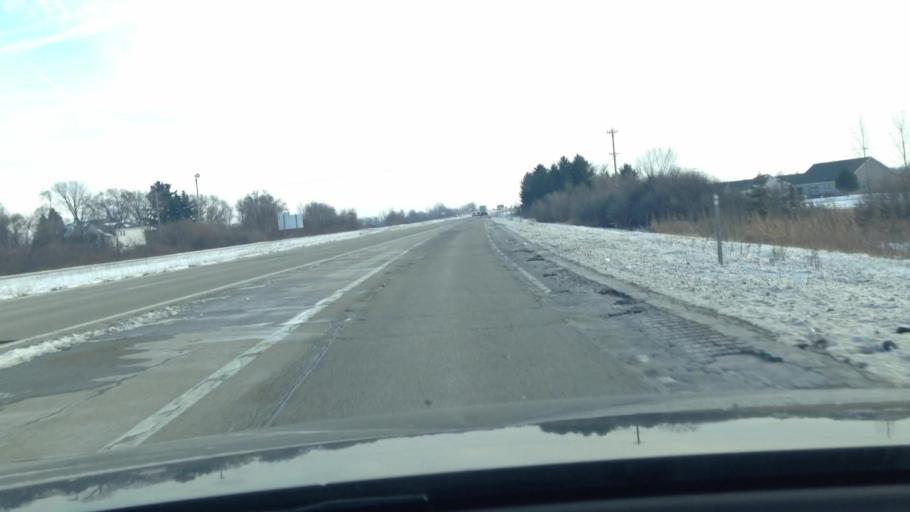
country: US
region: Wisconsin
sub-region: Walworth County
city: Elkhorn
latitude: 42.6641
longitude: -88.5149
